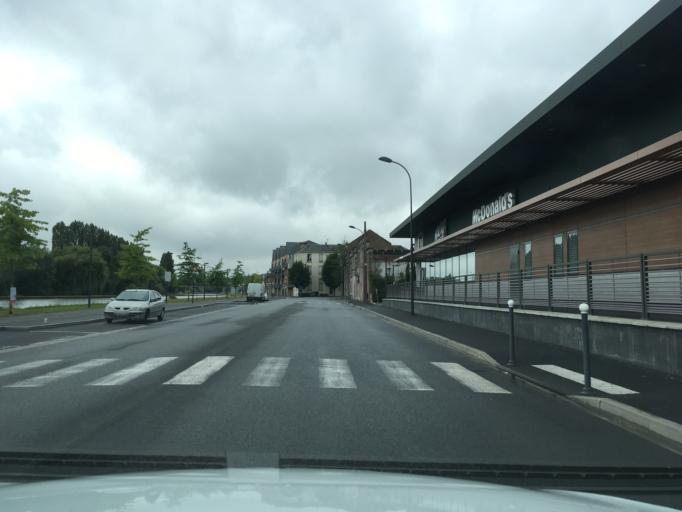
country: FR
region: Picardie
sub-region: Departement de l'Aisne
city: Saint-Quentin
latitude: 49.8399
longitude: 3.2904
